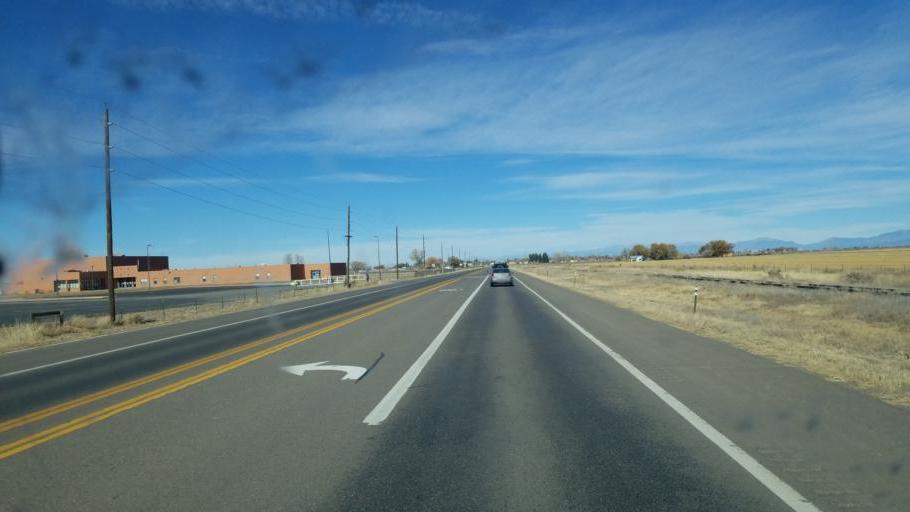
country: US
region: Colorado
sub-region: Conejos County
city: Conejos
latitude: 37.2468
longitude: -105.9685
